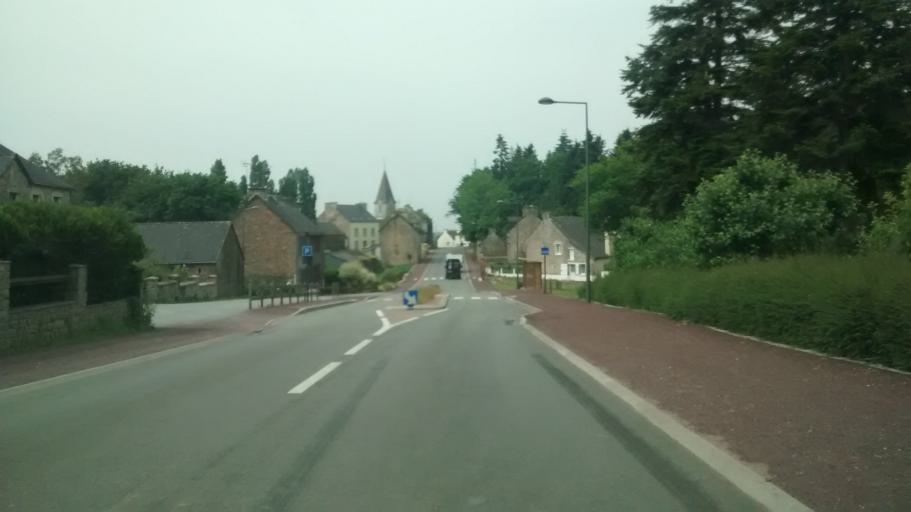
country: FR
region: Brittany
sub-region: Departement du Morbihan
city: Augan
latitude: 47.8740
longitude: -2.2066
